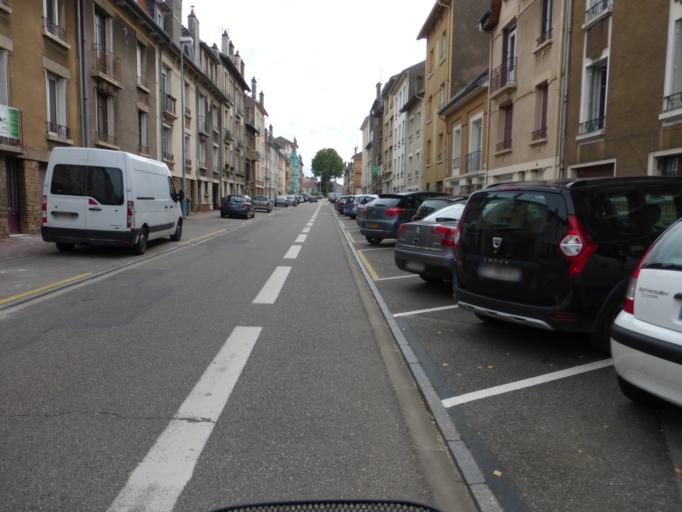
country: FR
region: Lorraine
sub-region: Departement de Meurthe-et-Moselle
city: Nancy
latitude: 48.6714
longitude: 6.1760
